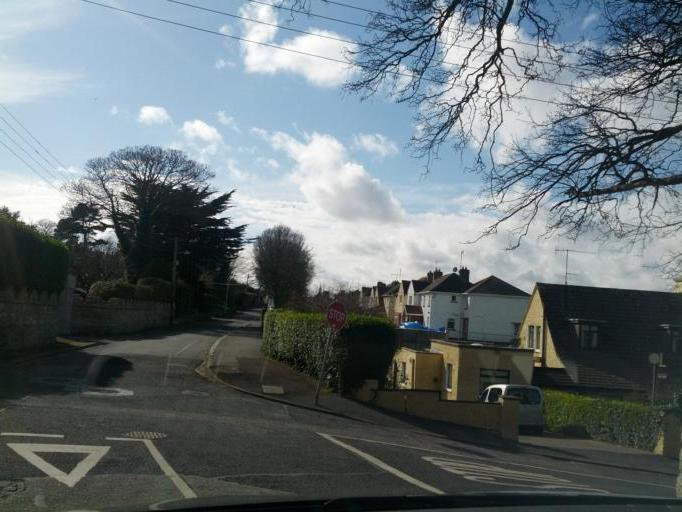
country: IE
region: Leinster
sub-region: Fingal County
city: Howth
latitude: 53.3845
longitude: -6.0598
